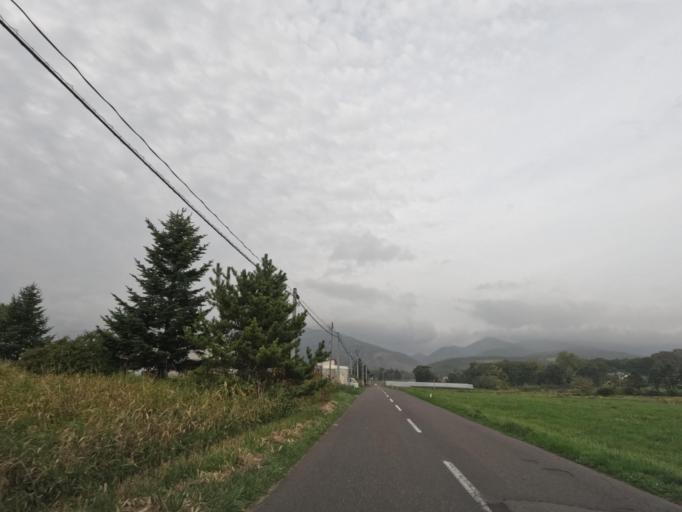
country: JP
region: Hokkaido
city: Date
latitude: 42.4242
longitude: 140.9098
